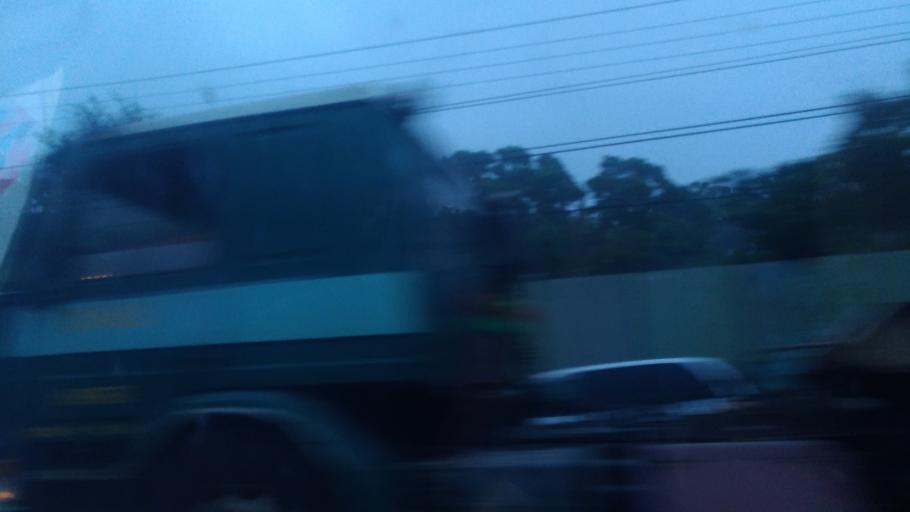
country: TW
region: Taiwan
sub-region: Miaoli
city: Miaoli
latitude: 24.5666
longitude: 120.7112
